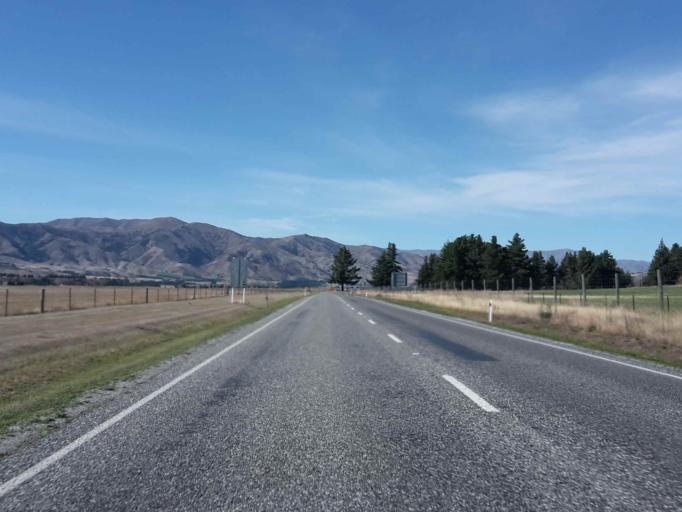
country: NZ
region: Otago
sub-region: Queenstown-Lakes District
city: Wanaka
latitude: -44.7257
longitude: 169.2462
